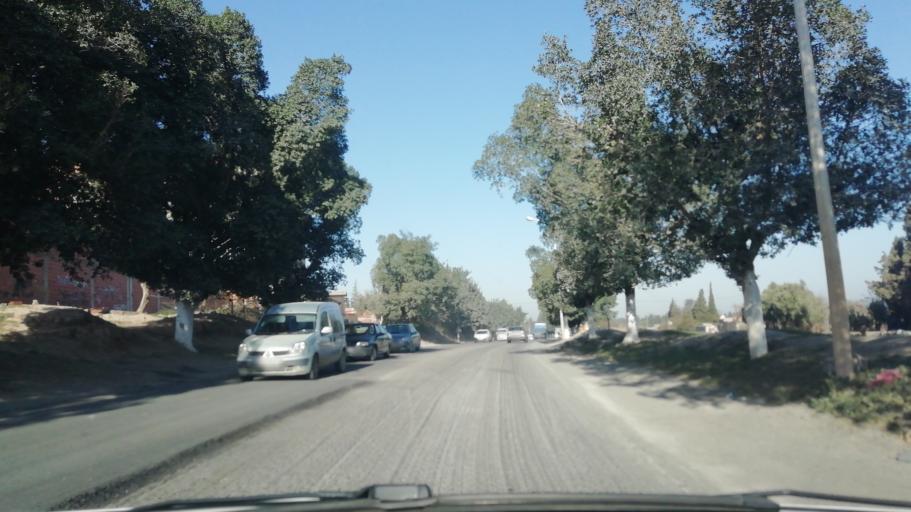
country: DZ
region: Mascara
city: Mascara
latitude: 35.5831
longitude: 0.0445
